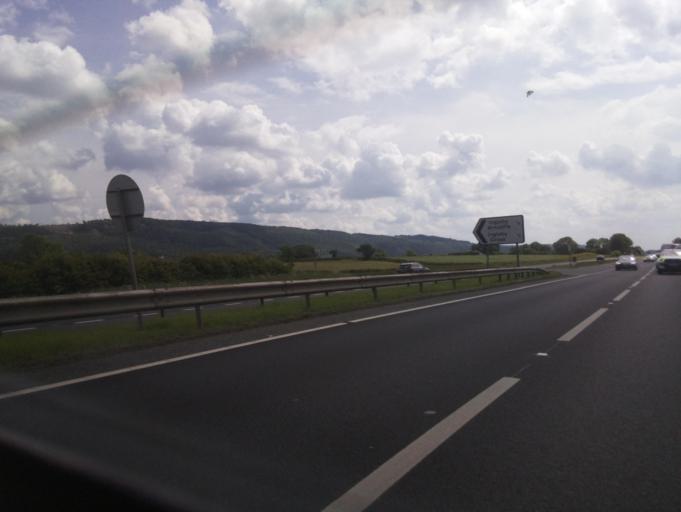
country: GB
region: England
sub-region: Stockton-on-Tees
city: Yarm
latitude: 54.4042
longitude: -1.3200
